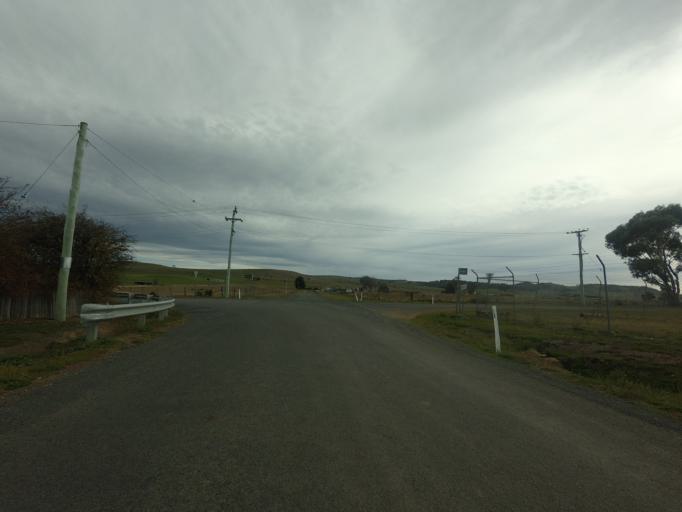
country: AU
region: Tasmania
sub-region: Derwent Valley
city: New Norfolk
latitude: -42.3834
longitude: 146.9860
